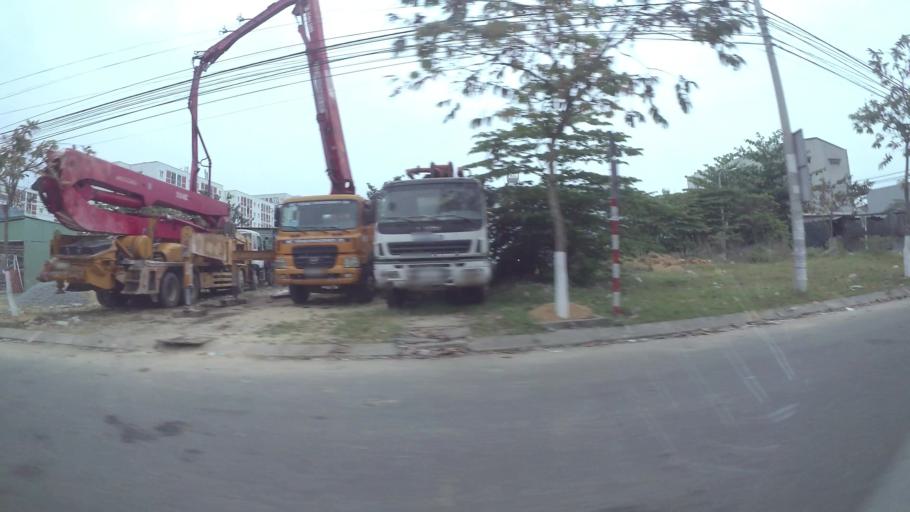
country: VN
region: Da Nang
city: Thanh Khe
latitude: 16.0438
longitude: 108.1768
